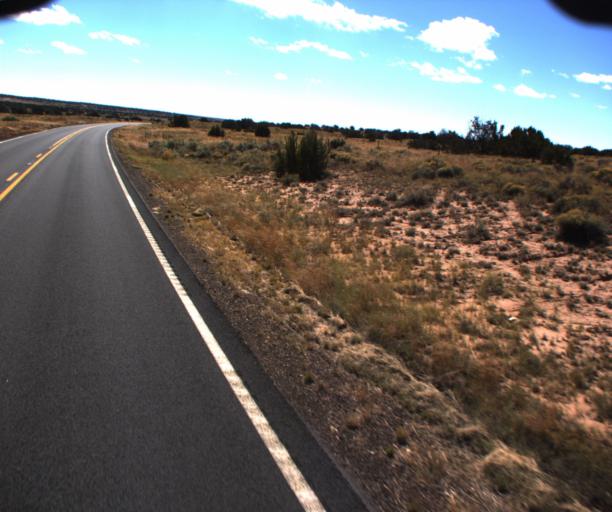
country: US
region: Arizona
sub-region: Apache County
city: Houck
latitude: 35.0069
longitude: -109.2298
